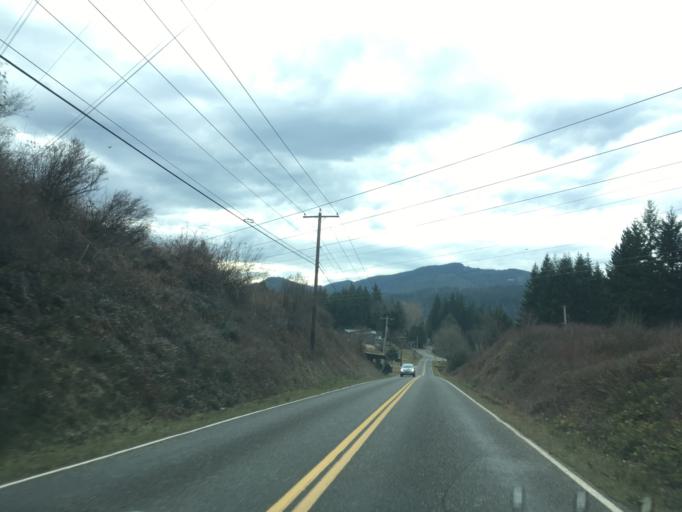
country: US
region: Washington
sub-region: Whatcom County
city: Sudden Valley
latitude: 48.7604
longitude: -122.3554
